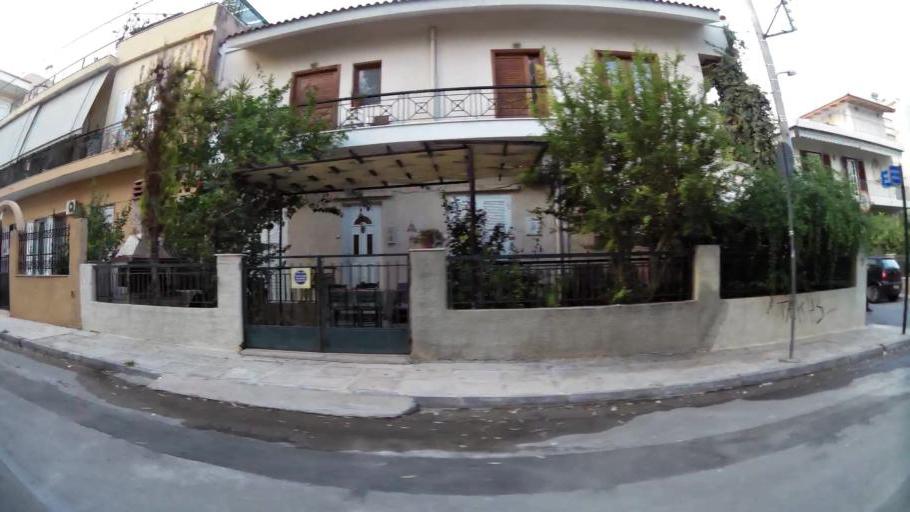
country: GR
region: Attica
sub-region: Nomarchia Athinas
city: Ilion
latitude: 38.0269
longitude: 23.6918
